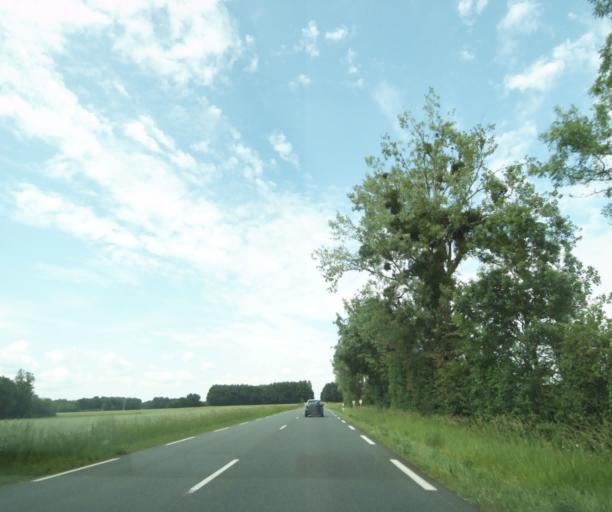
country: FR
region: Pays de la Loire
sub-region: Departement de Maine-et-Loire
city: Montreuil-Bellay
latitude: 47.1675
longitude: -0.1402
